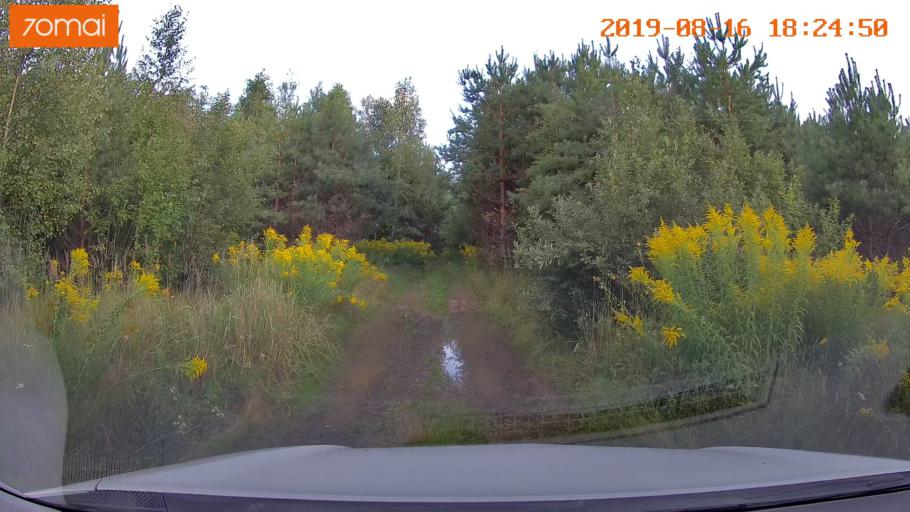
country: BY
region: Mogilev
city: Asipovichy
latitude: 53.2043
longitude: 28.6373
